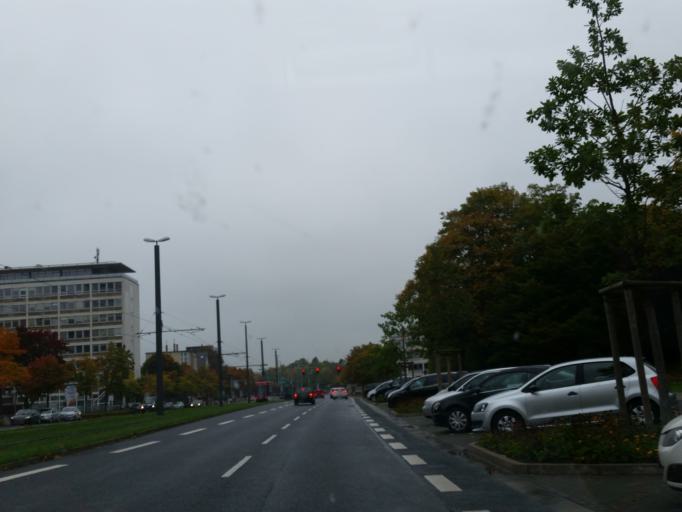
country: DE
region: Lower Saxony
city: Braunschweig
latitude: 52.2555
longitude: 10.5356
